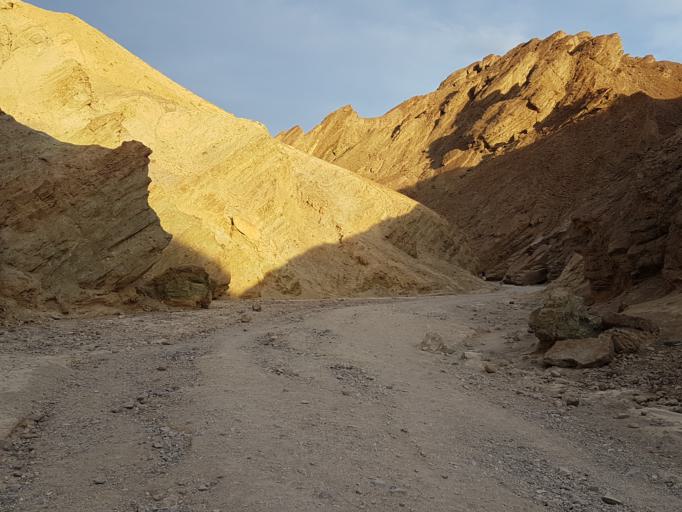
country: US
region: Nevada
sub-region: Nye County
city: Beatty
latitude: 36.4219
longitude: -116.8452
